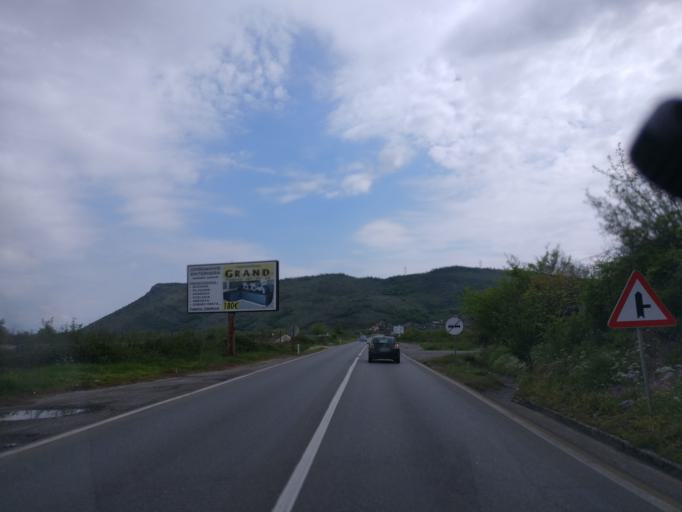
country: ME
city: Spuz
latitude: 42.4697
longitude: 19.1740
